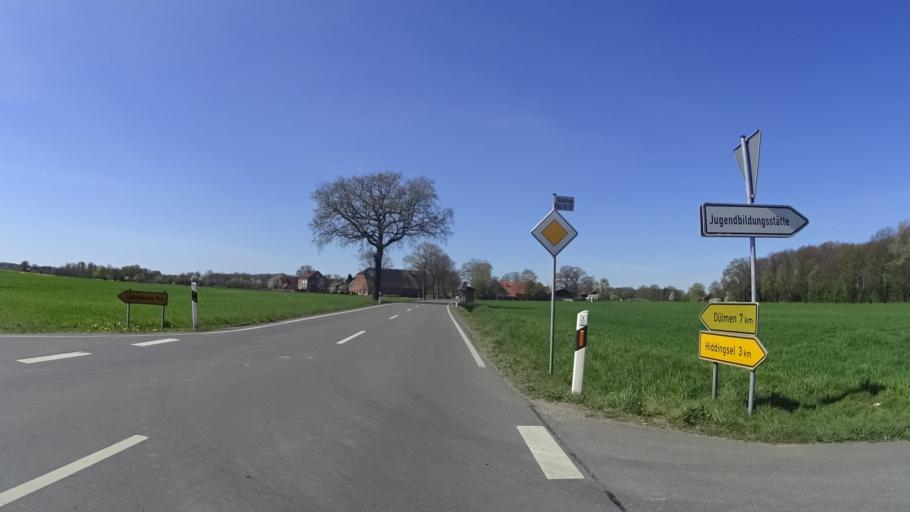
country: DE
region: North Rhine-Westphalia
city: Ludinghausen
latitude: 51.8215
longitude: 7.3727
